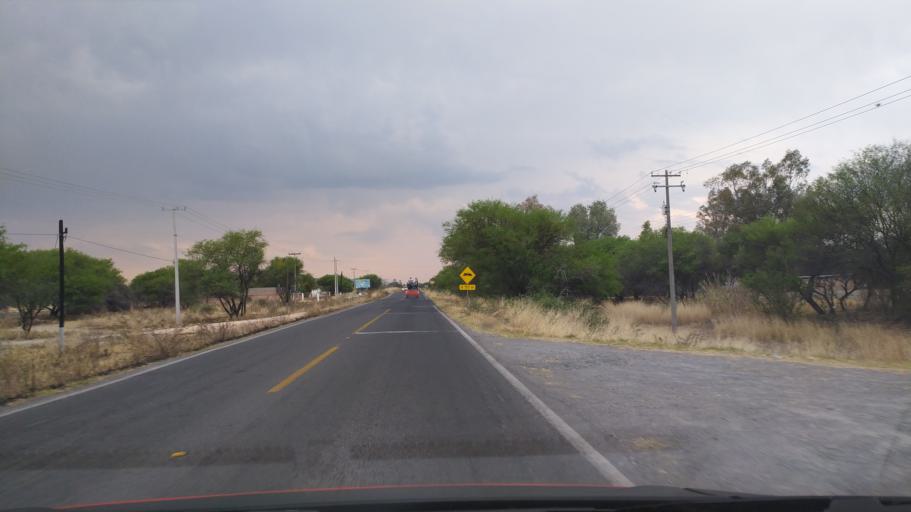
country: MX
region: Guanajuato
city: Ciudad Manuel Doblado
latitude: 20.7972
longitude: -101.9058
